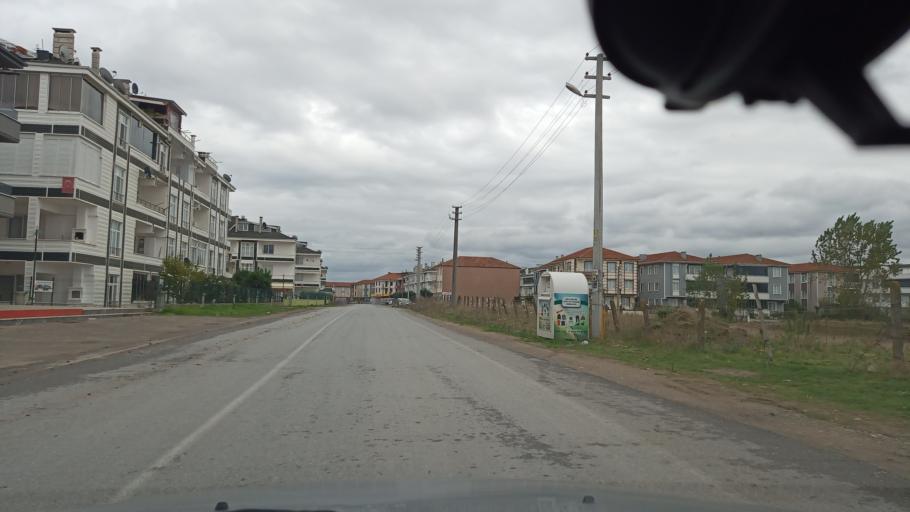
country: TR
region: Sakarya
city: Karasu
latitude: 41.1118
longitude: 30.6776
